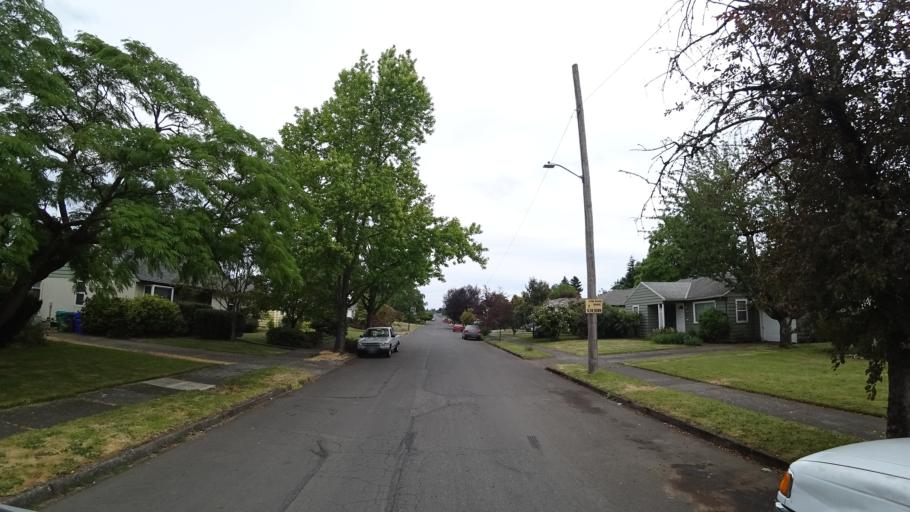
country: US
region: Oregon
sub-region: Multnomah County
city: Lents
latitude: 45.5108
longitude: -122.5712
